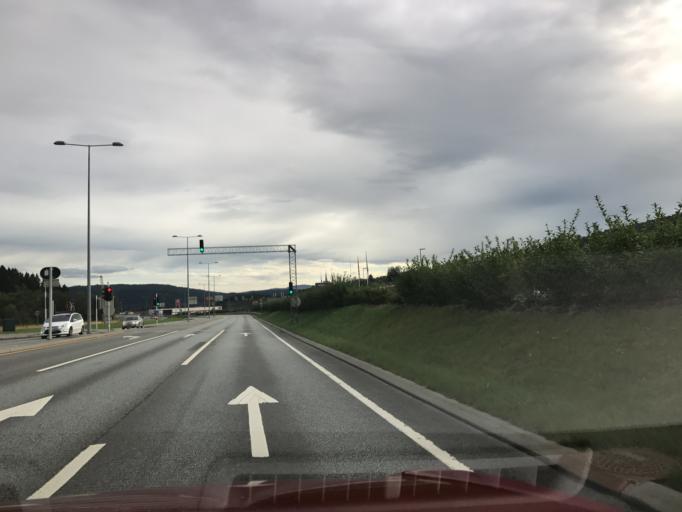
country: NO
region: Hordaland
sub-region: Bergen
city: Hylkje
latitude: 60.4815
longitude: 5.3708
